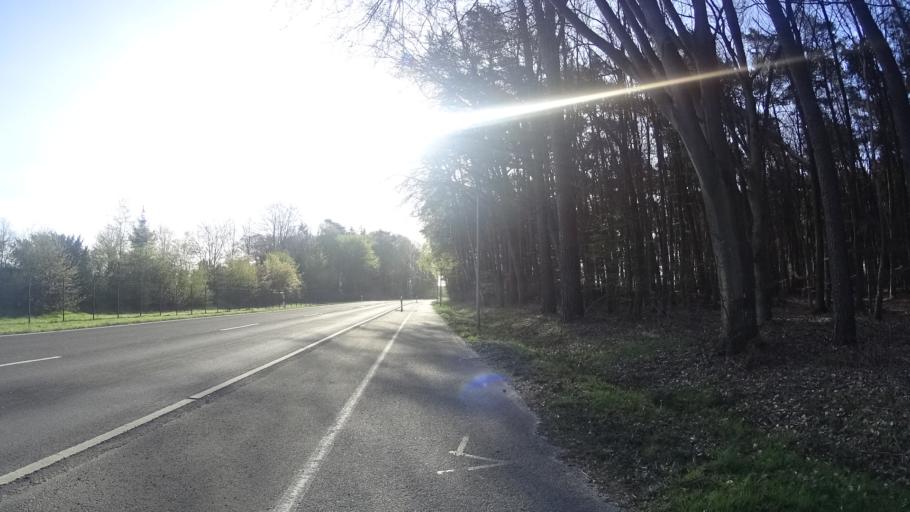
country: DE
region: North Rhine-Westphalia
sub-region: Regierungsbezirk Munster
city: Greven
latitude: 52.1128
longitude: 7.5732
